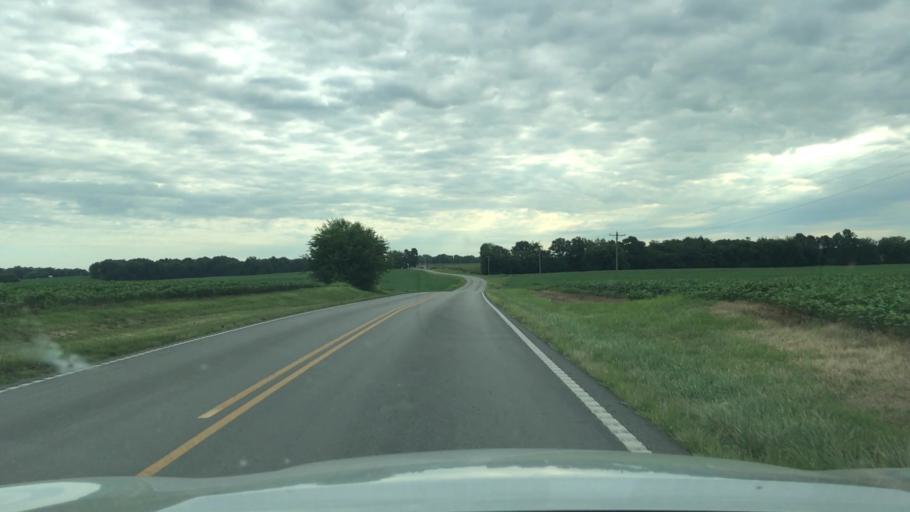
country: US
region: Kentucky
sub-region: Todd County
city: Elkton
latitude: 36.7399
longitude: -87.1826
